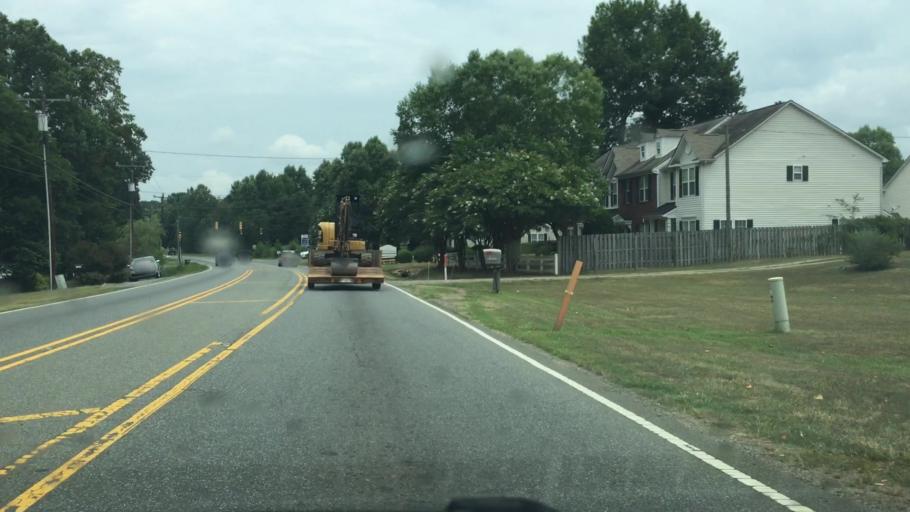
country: US
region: North Carolina
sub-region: Iredell County
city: Mooresville
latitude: 35.6241
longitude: -80.8247
